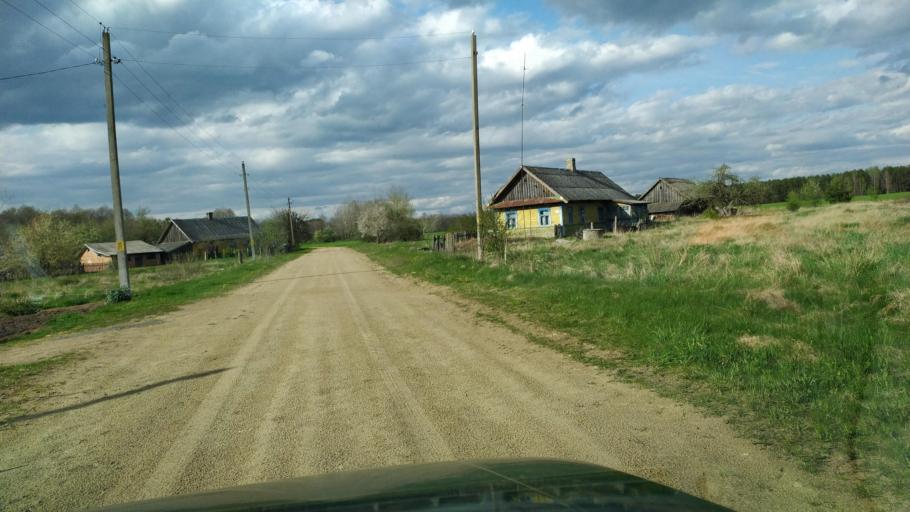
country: BY
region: Brest
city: Pruzhany
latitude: 52.7092
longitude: 24.2592
